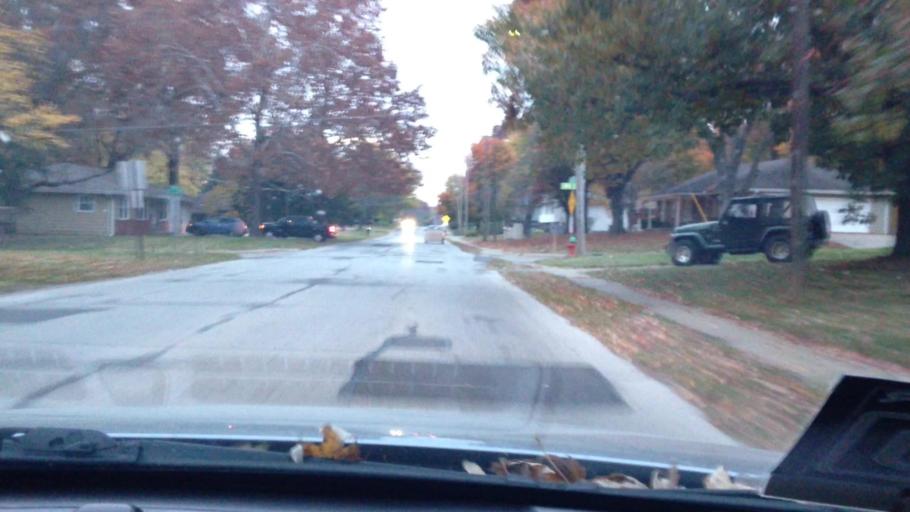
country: US
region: Kansas
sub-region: Leavenworth County
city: Leavenworth
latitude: 39.2906
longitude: -94.9366
